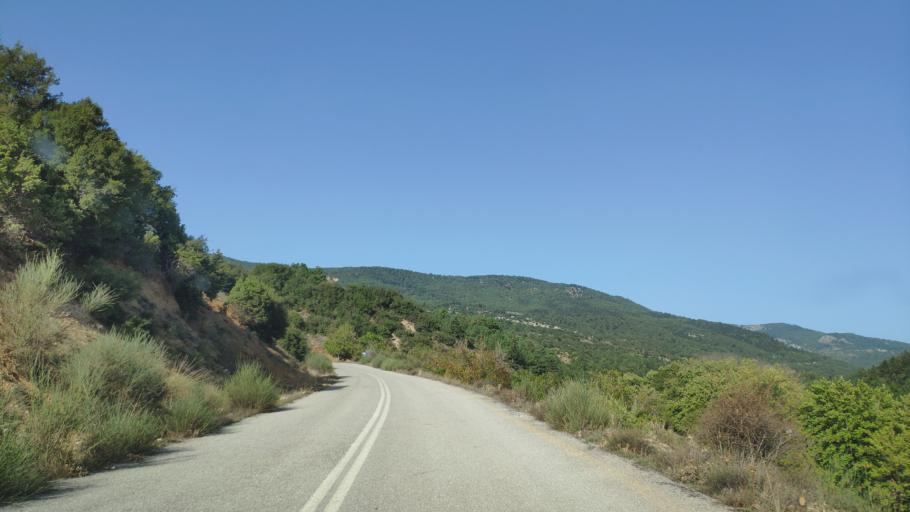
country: GR
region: West Greece
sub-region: Nomos Achaias
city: Aiyira
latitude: 37.9891
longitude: 22.3626
